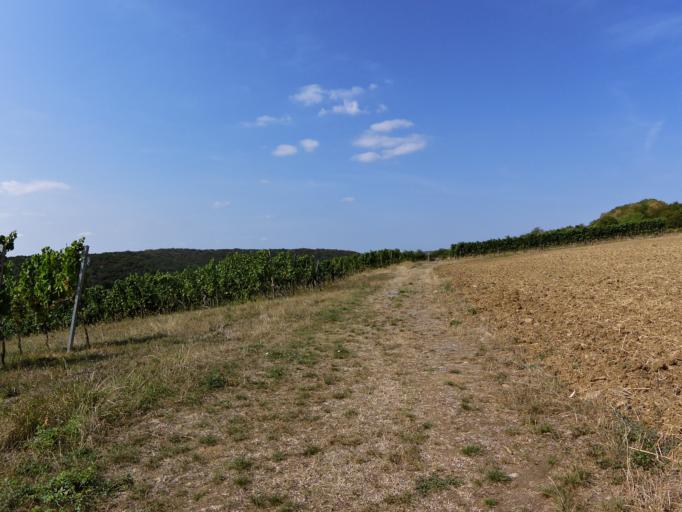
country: DE
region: Bavaria
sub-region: Regierungsbezirk Unterfranken
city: Theilheim
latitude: 49.7565
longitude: 10.0135
